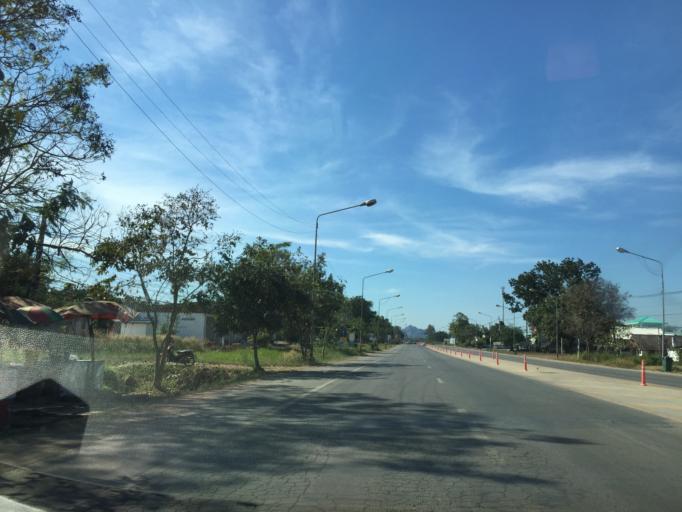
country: TH
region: Changwat Nong Bua Lamphu
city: Na Wang
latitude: 17.3241
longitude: 102.0768
